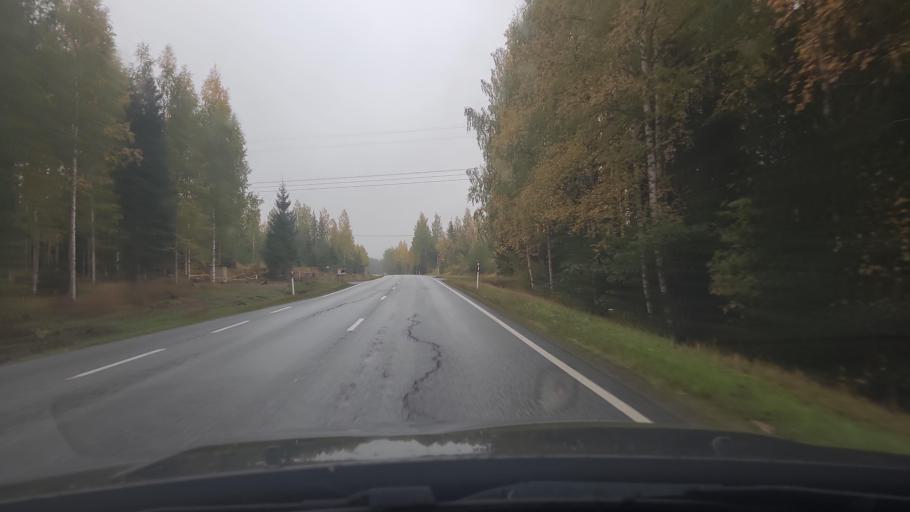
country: FI
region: Northern Savo
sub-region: Varkaus
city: Kangaslampi
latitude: 62.4594
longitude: 28.3235
